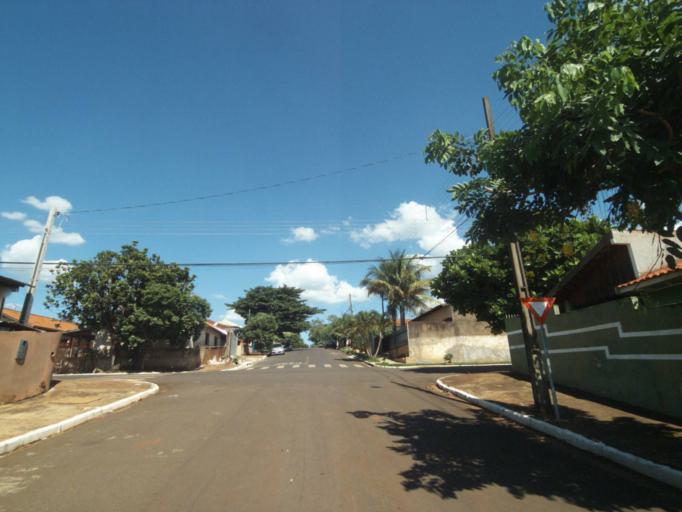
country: BR
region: Parana
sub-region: Sertanopolis
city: Sertanopolis
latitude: -23.0407
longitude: -50.8198
